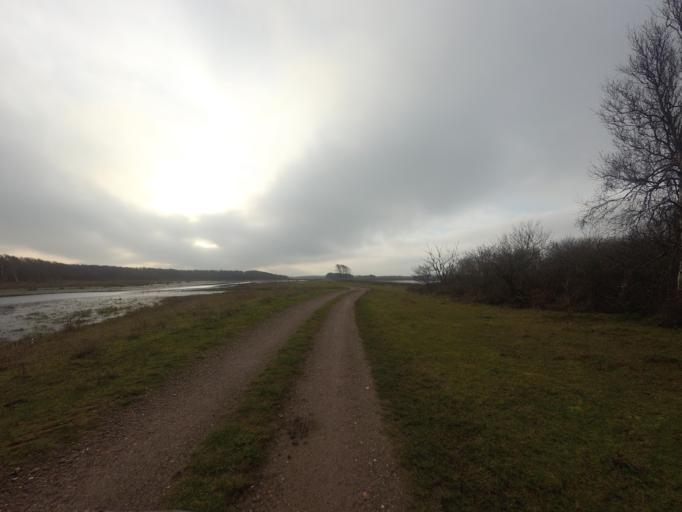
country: NL
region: North Holland
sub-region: Gemeente Texel
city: Den Burg
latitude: 53.1180
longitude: 4.7954
